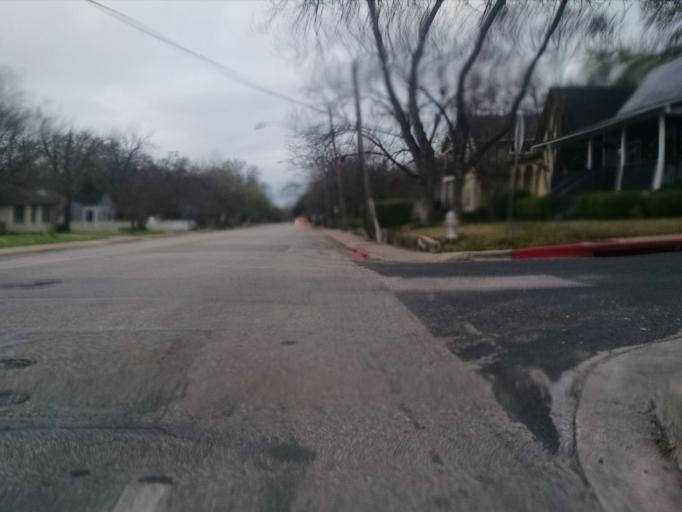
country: US
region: Texas
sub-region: Travis County
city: Austin
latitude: 30.3110
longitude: -97.7221
